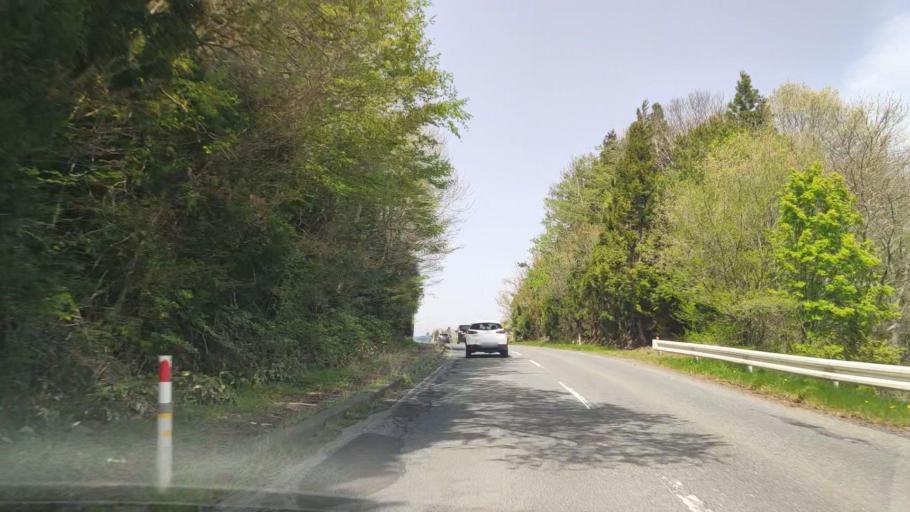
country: JP
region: Aomori
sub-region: Misawa Shi
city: Inuotose
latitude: 40.5892
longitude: 141.3515
